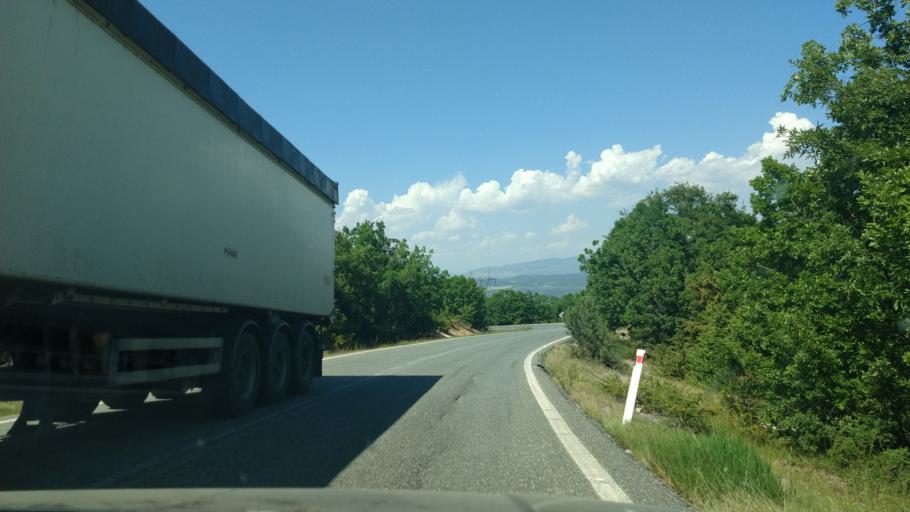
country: GR
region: West Macedonia
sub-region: Nomos Grevenon
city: Grevena
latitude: 40.0192
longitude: 21.4870
